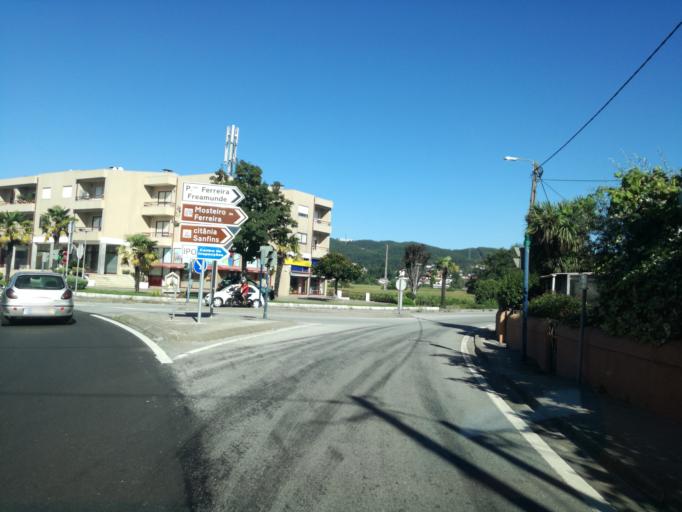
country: PT
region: Porto
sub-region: Valongo
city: Alfena
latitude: 41.2596
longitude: -8.4839
